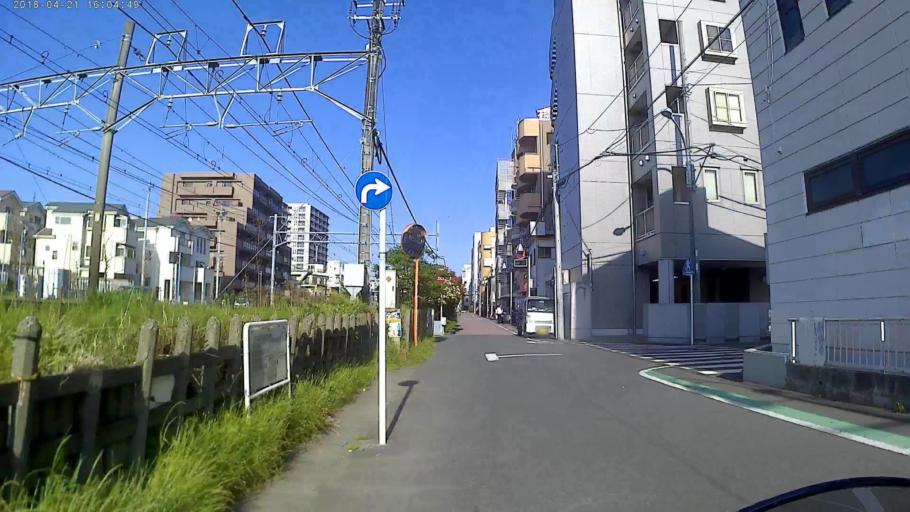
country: JP
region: Kanagawa
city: Fujisawa
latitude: 35.3365
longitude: 139.4417
